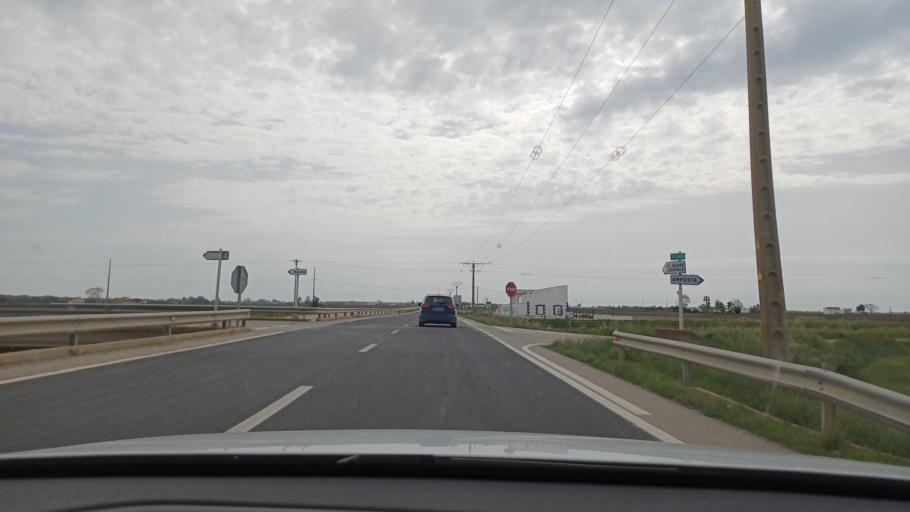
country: ES
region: Catalonia
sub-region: Provincia de Tarragona
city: Deltebre
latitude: 40.7097
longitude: 0.6835
